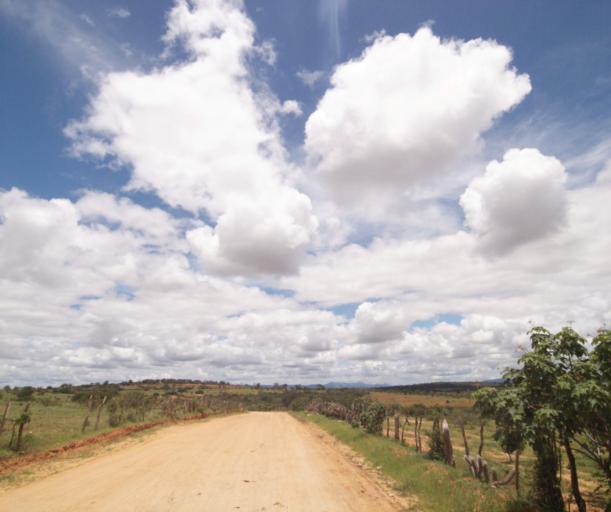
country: BR
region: Bahia
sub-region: Tanhacu
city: Tanhacu
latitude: -14.1610
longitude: -41.1739
